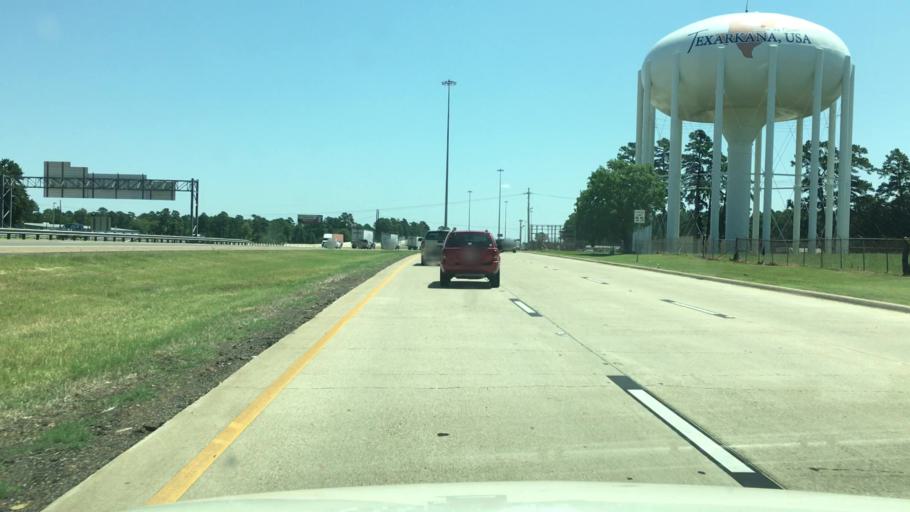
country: US
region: Arkansas
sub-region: Miller County
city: Texarkana
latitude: 33.4692
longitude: -94.0555
